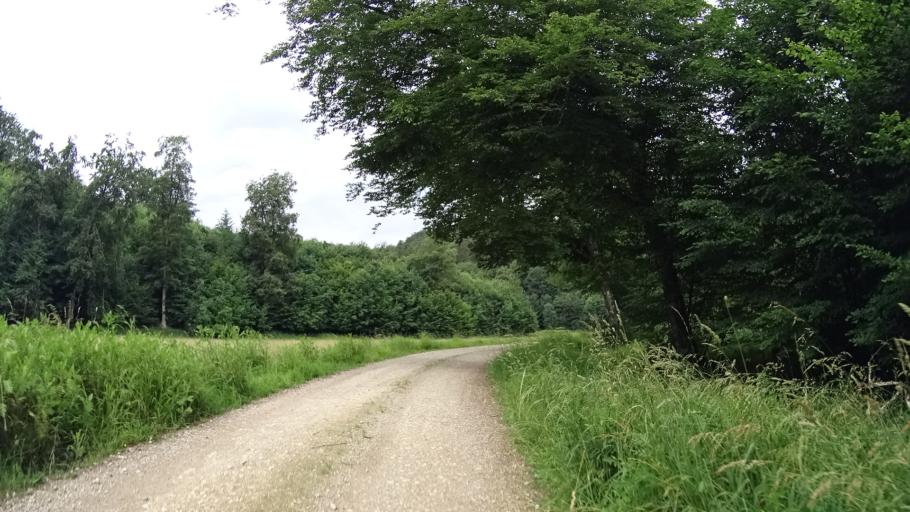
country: DE
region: Bavaria
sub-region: Upper Bavaria
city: Denkendorf
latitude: 48.9179
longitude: 11.5183
